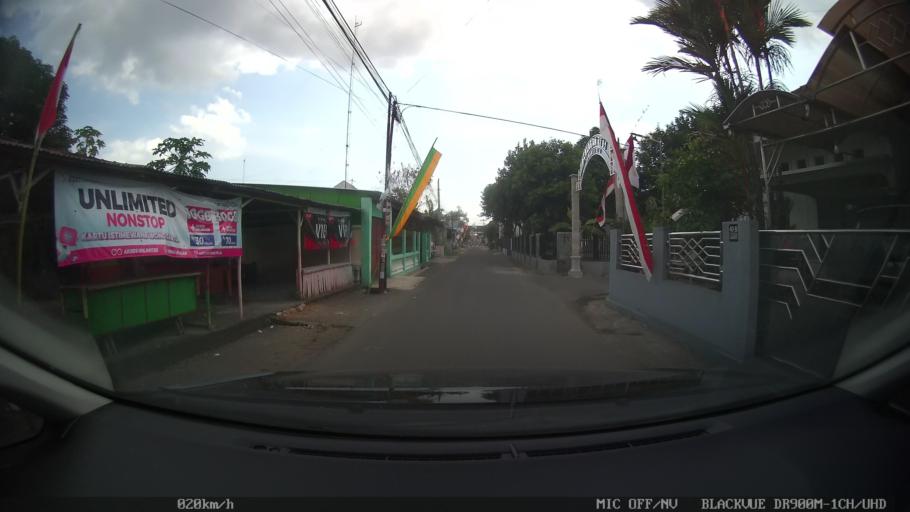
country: ID
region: Daerah Istimewa Yogyakarta
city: Gamping Lor
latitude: -7.8072
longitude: 110.3261
